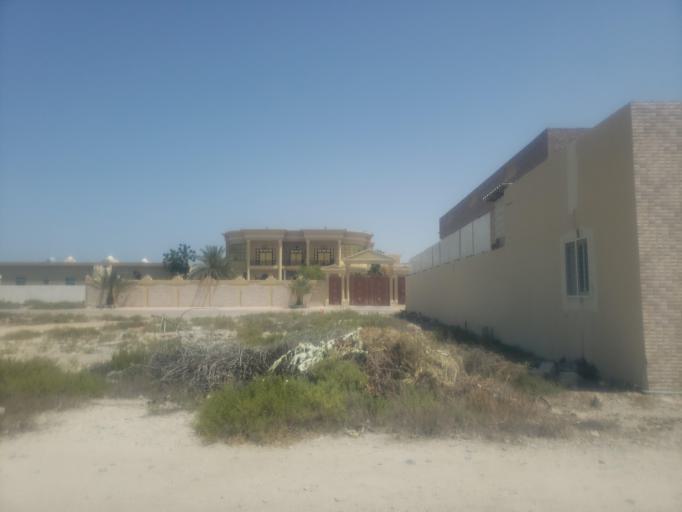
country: AE
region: Ra's al Khaymah
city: Ras al-Khaimah
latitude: 25.8094
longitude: 55.9568
